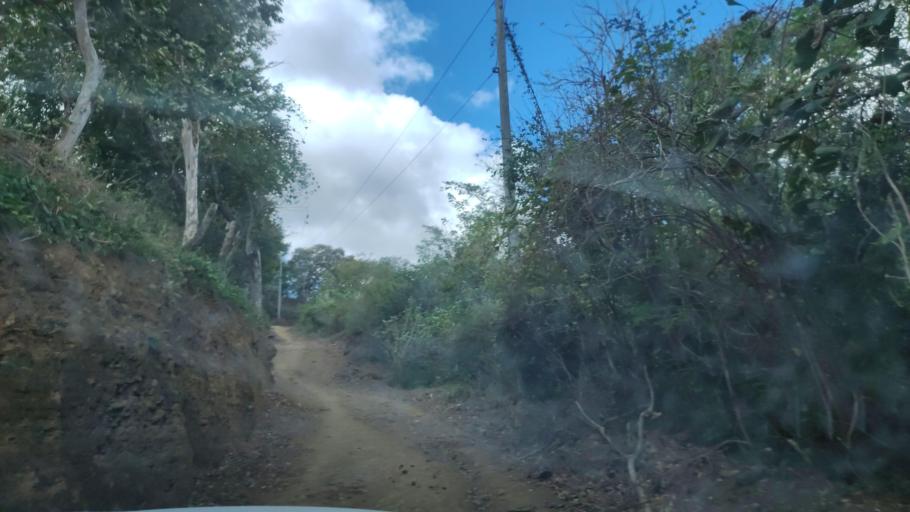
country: NI
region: Carazo
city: Santa Teresa
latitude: 11.6520
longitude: -86.2009
